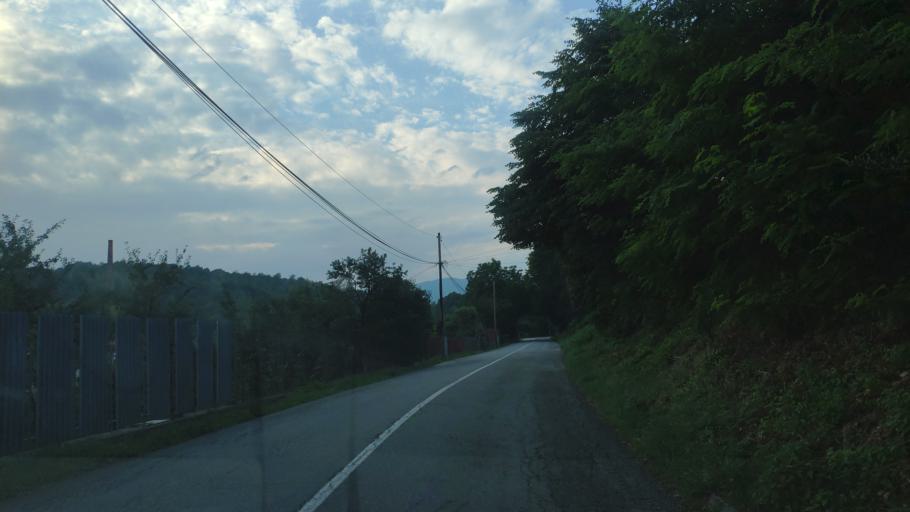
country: SK
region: Kosicky
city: Moldava nad Bodvou
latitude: 48.6852
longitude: 20.9752
